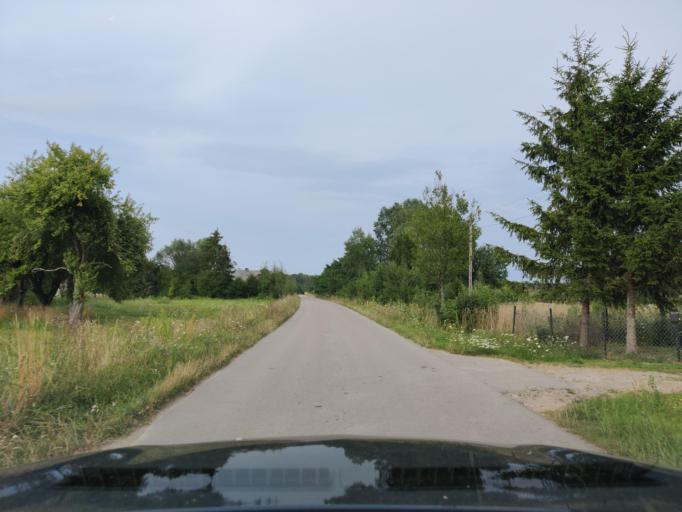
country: PL
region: Masovian Voivodeship
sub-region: Powiat pultuski
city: Obryte
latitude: 52.6952
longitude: 21.2013
